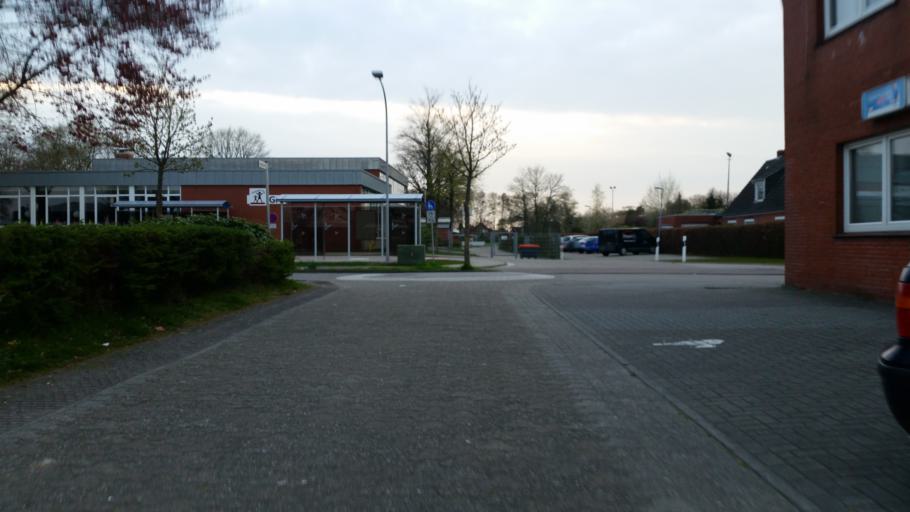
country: DE
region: Lower Saxony
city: Aurich
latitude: 53.4784
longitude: 7.4510
